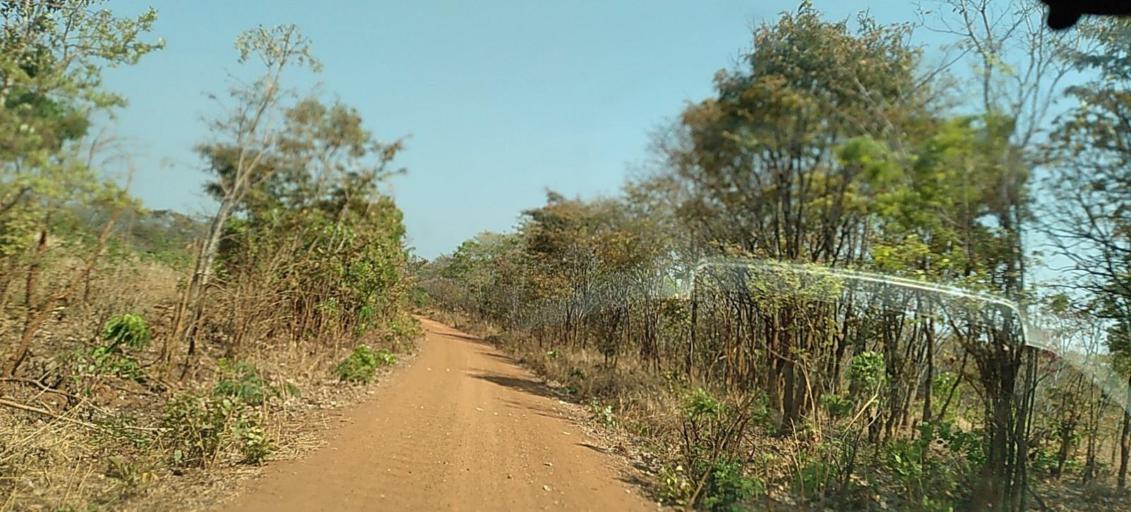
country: ZM
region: North-Western
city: Kasempa
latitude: -13.3905
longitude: 25.6855
